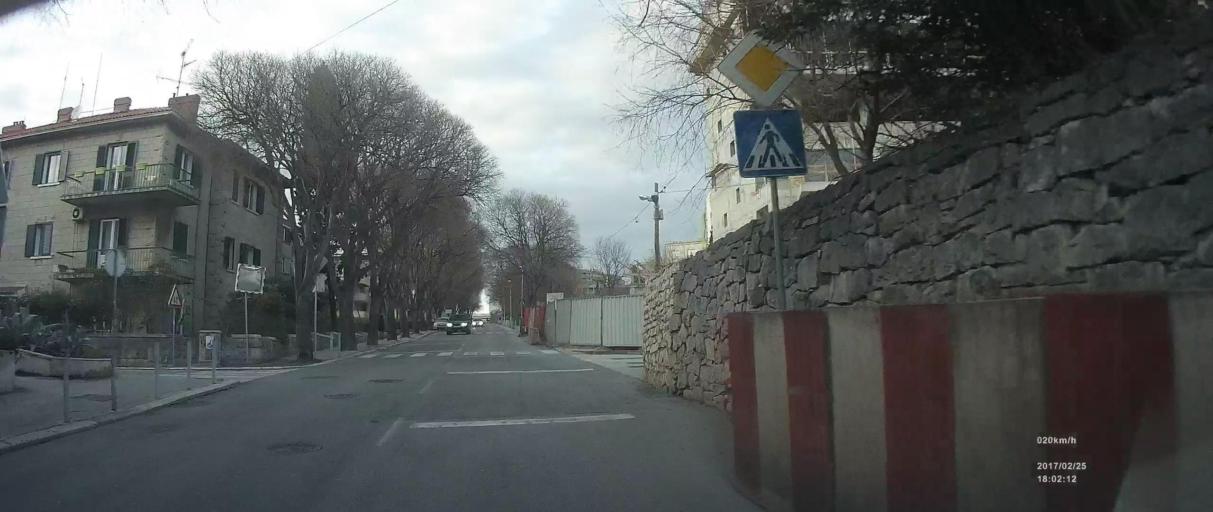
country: HR
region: Splitsko-Dalmatinska
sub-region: Grad Split
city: Split
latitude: 43.5023
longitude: 16.4571
